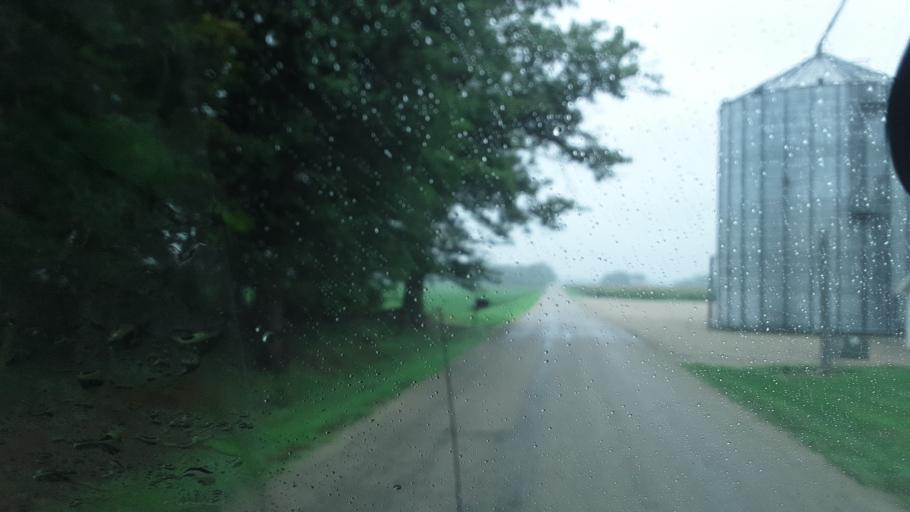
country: US
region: Indiana
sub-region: Adams County
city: Geneva
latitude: 40.6272
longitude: -85.0242
